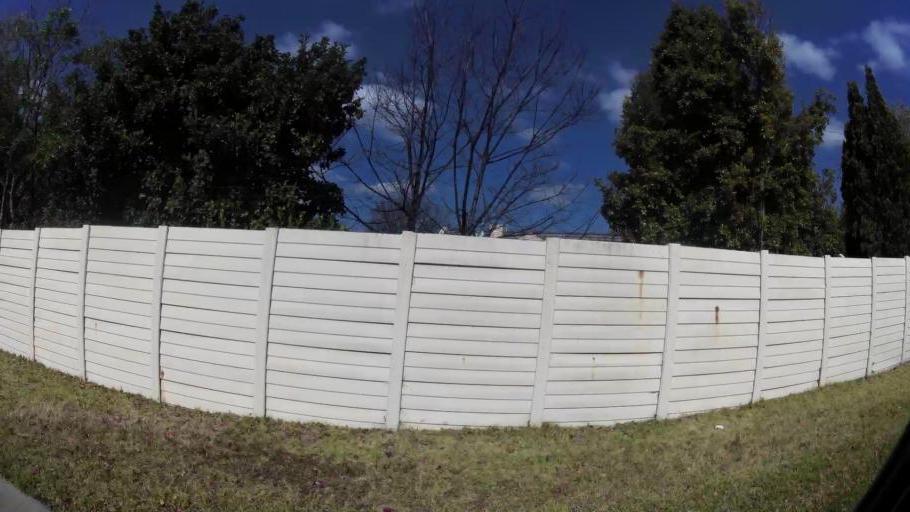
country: ZA
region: Gauteng
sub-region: West Rand District Municipality
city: Muldersdriseloop
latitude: -26.0599
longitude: 27.9681
